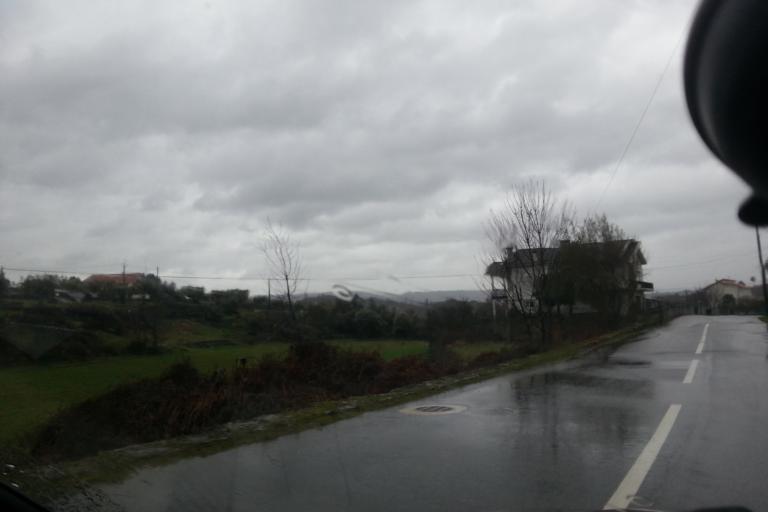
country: PT
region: Guarda
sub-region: Fornos de Algodres
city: Fornos de Algodres
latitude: 40.5692
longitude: -7.5123
